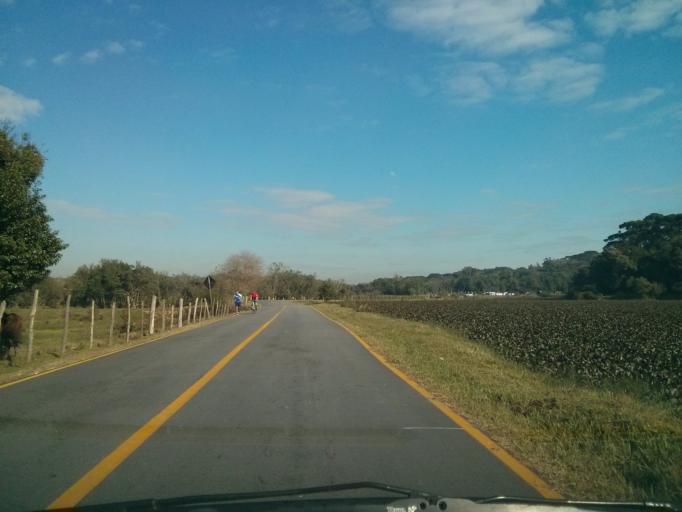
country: BR
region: Parana
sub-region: Sao Jose Dos Pinhais
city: Sao Jose dos Pinhais
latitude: -25.5600
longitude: -49.2267
